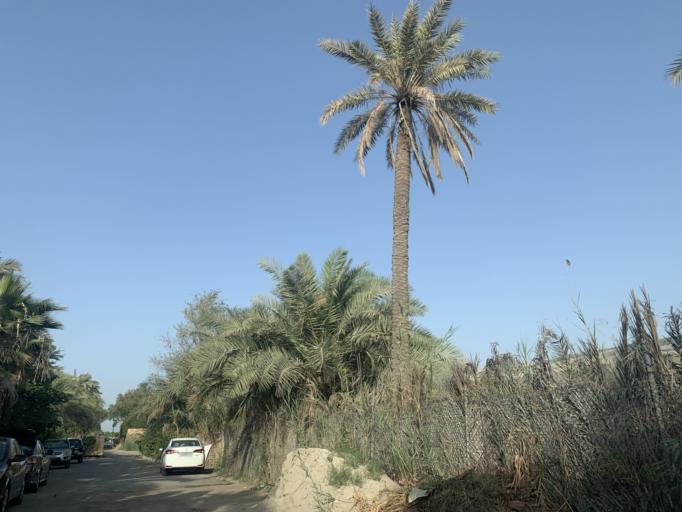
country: BH
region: Central Governorate
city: Madinat Hamad
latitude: 26.1877
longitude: 50.4592
